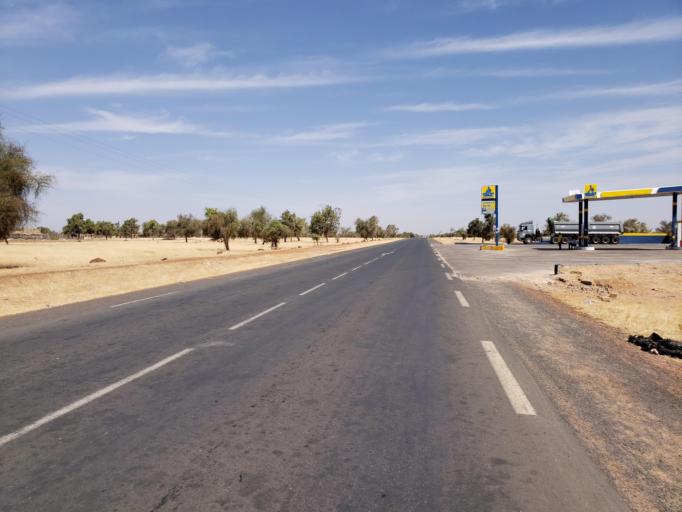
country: SN
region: Matam
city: Ranerou
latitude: 15.3060
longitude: -13.9505
